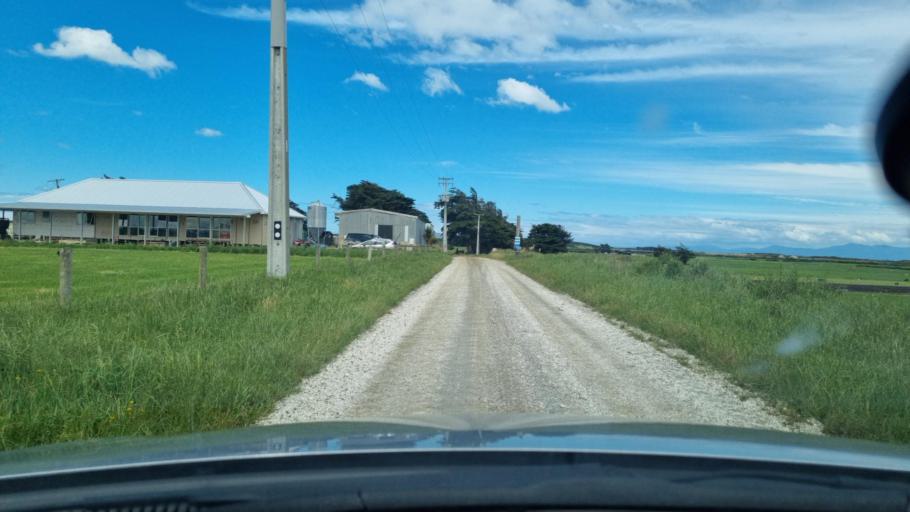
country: NZ
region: Southland
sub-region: Invercargill City
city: Invercargill
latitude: -46.3998
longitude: 168.2563
